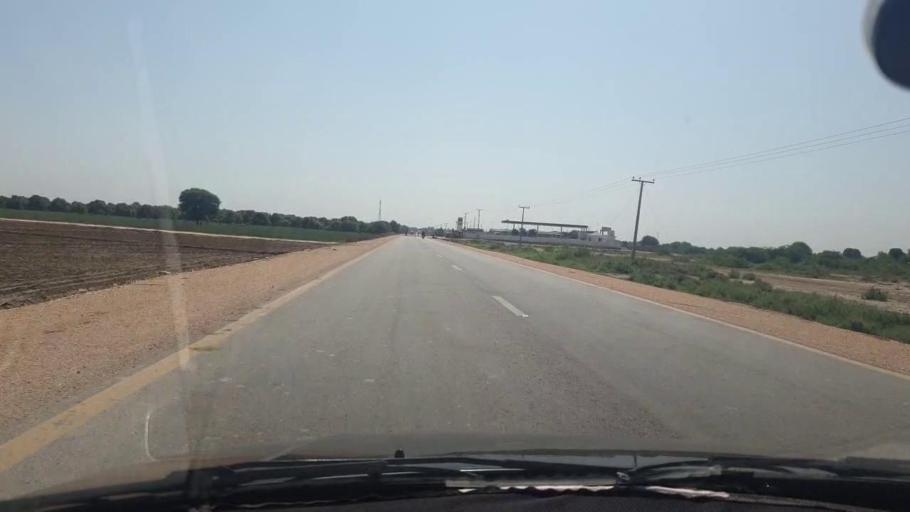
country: PK
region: Sindh
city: Chambar
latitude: 25.3111
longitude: 68.8062
